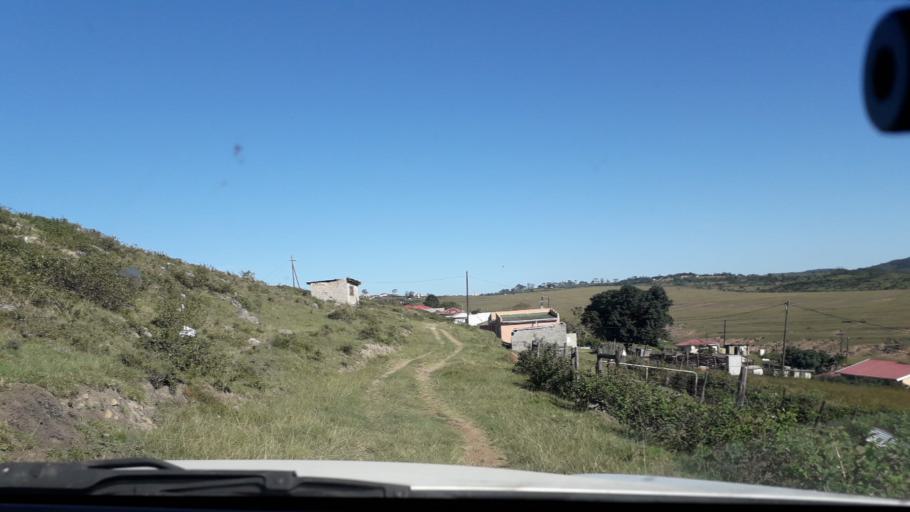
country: ZA
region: Eastern Cape
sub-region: Buffalo City Metropolitan Municipality
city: East London
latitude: -32.8379
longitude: 27.9976
